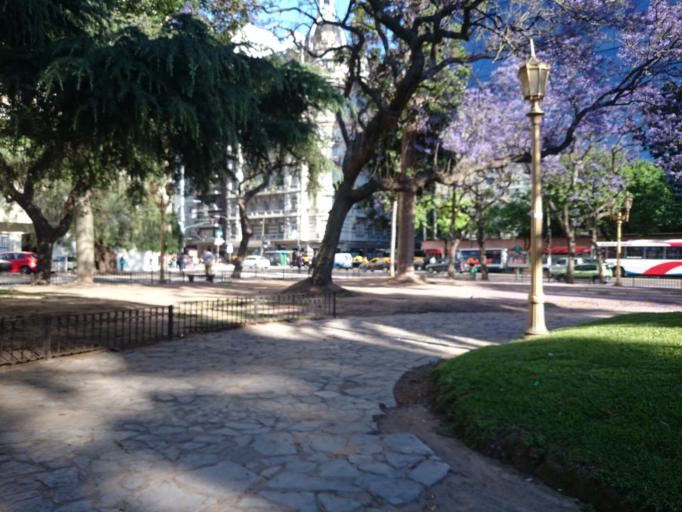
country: AR
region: Buenos Aires F.D.
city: Buenos Aires
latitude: -34.5996
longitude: -58.3849
